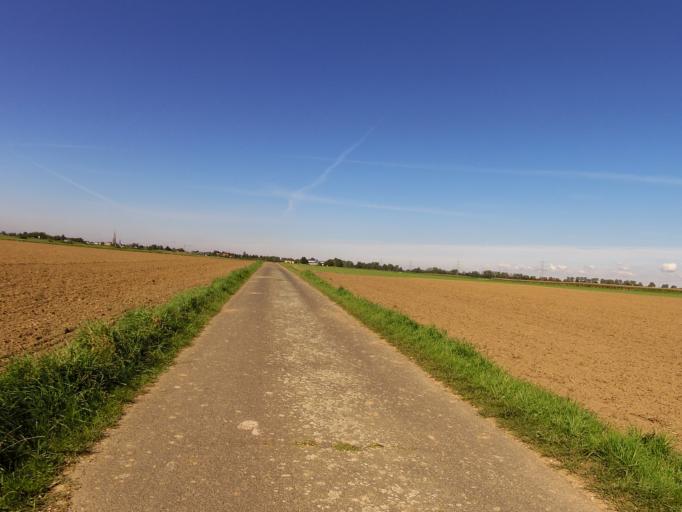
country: DE
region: North Rhine-Westphalia
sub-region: Regierungsbezirk Koln
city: Rheinbach
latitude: 50.6435
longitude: 6.9032
